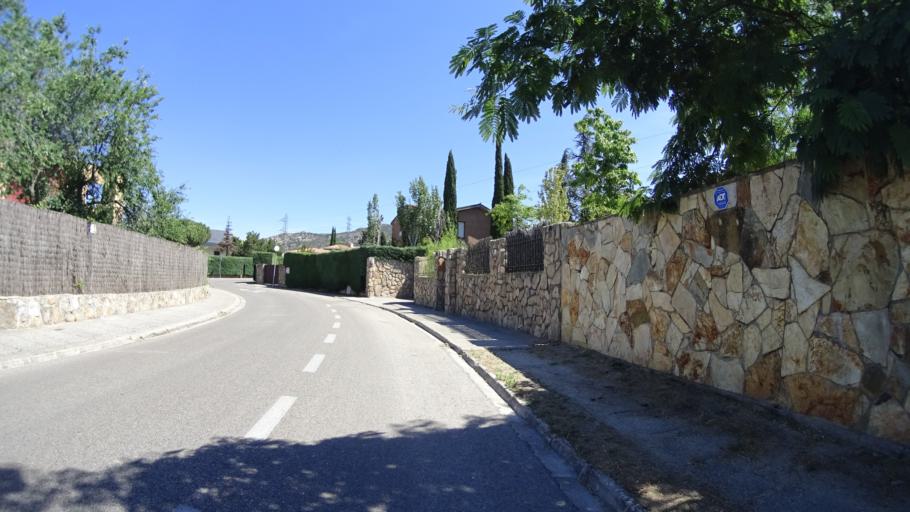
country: ES
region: Madrid
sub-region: Provincia de Madrid
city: Hoyo de Manzanares
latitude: 40.6125
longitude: -3.9350
